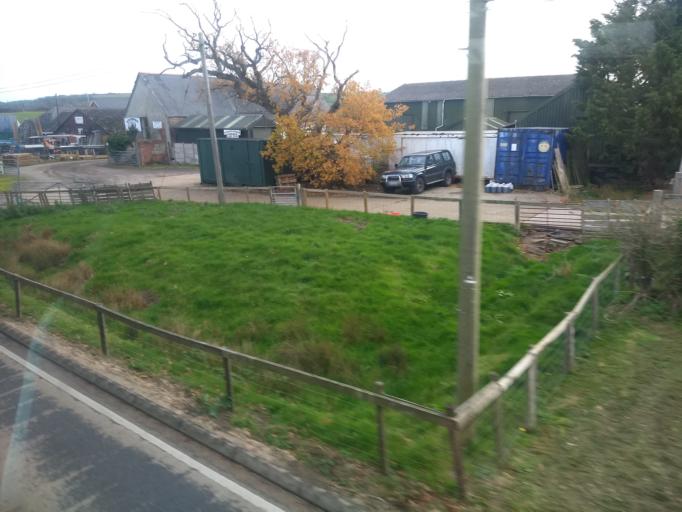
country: GB
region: England
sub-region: Isle of Wight
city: Northwood
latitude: 50.7025
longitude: -1.3515
